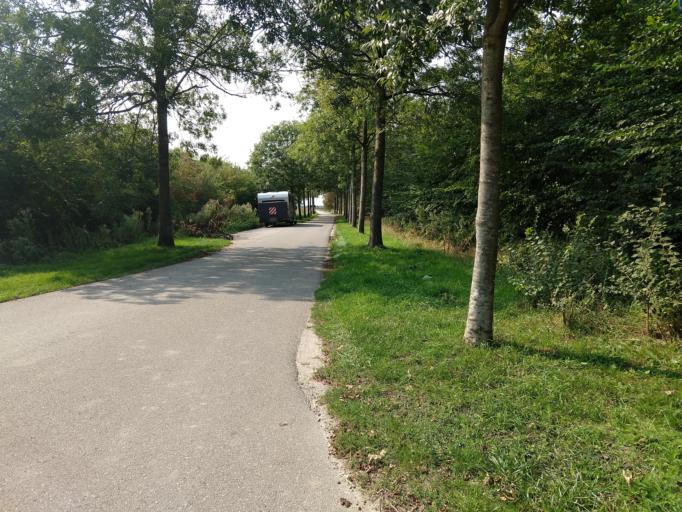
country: NL
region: Zeeland
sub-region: Schouwen-Duiveland
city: Renesse
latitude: 51.7202
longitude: 3.7930
